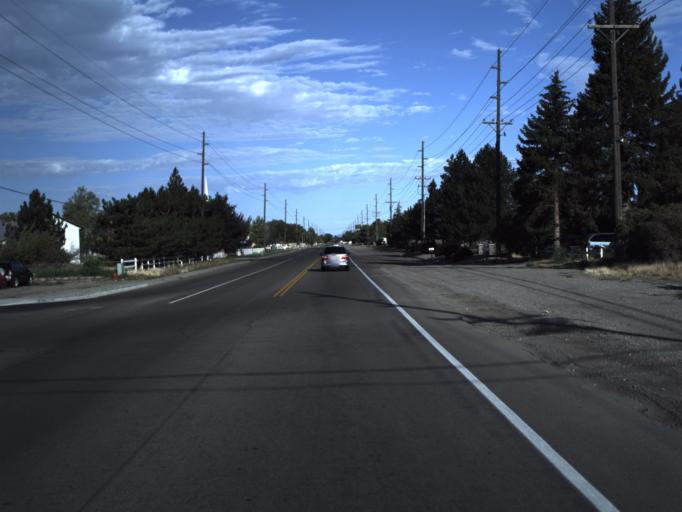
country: US
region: Utah
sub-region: Utah County
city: Spanish Fork
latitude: 40.0961
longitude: -111.6162
